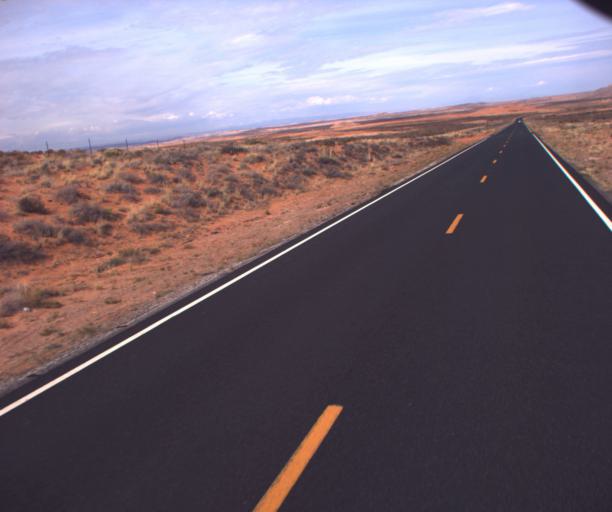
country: US
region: Arizona
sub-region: Apache County
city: Many Farms
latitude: 36.9028
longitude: -109.6249
